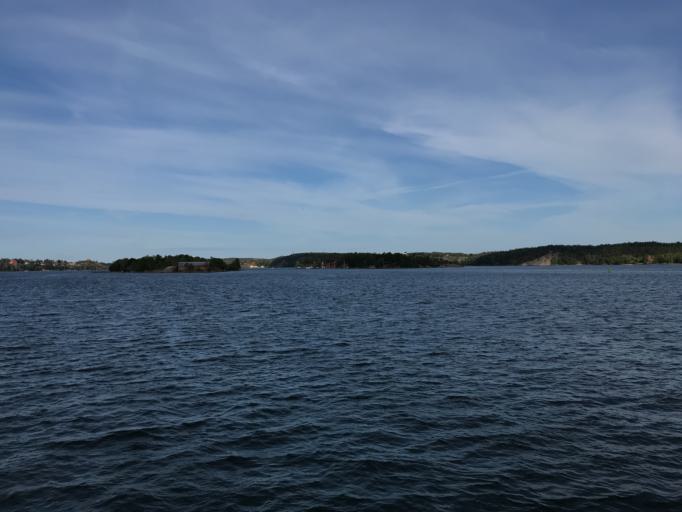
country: SE
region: Stockholm
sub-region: Nacka Kommun
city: Nacka
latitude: 59.3291
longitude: 18.1569
